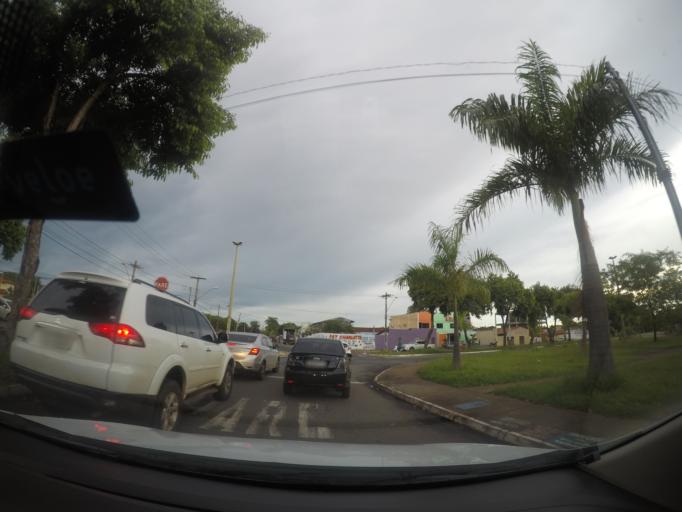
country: BR
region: Goias
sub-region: Goiania
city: Goiania
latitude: -16.7168
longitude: -49.3105
